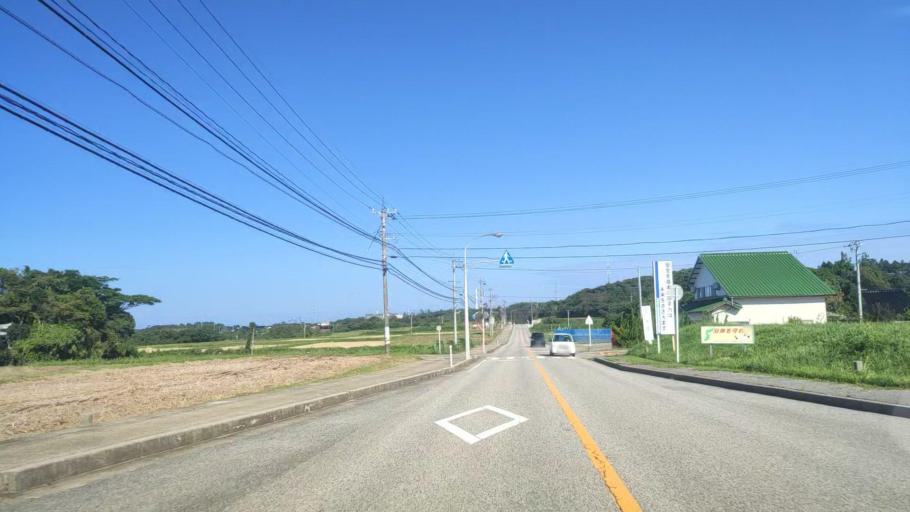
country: JP
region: Ishikawa
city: Hakui
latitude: 37.0456
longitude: 136.7384
